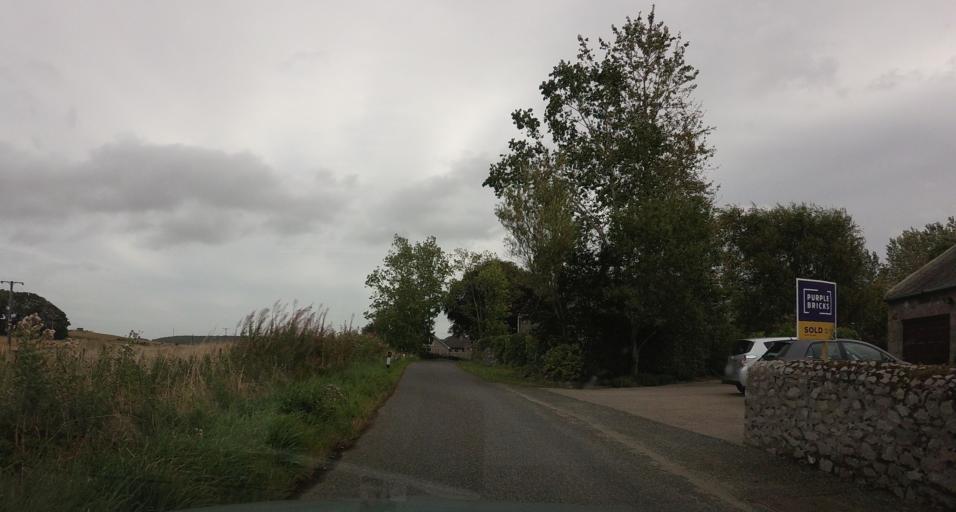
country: GB
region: Scotland
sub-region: Aberdeenshire
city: Kemnay
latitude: 57.2184
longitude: -2.4642
